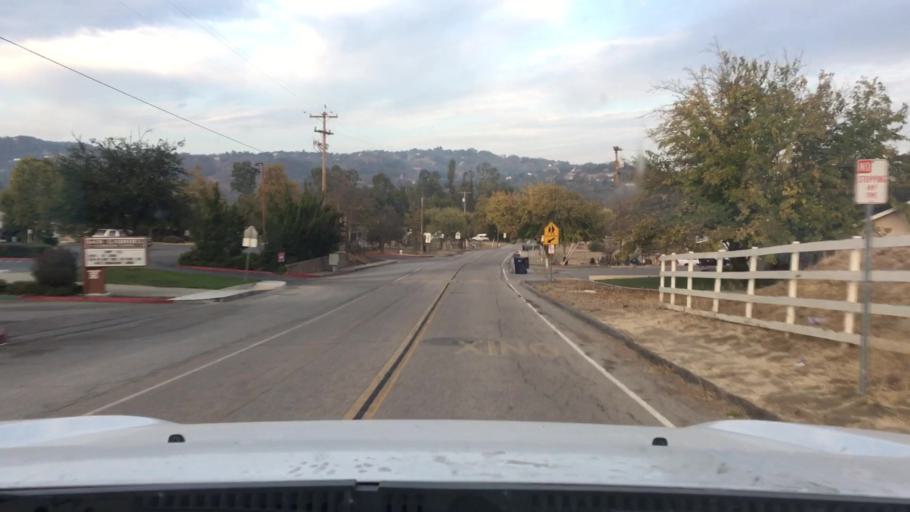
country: US
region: California
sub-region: San Luis Obispo County
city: Atascadero
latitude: 35.4592
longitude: -120.6683
